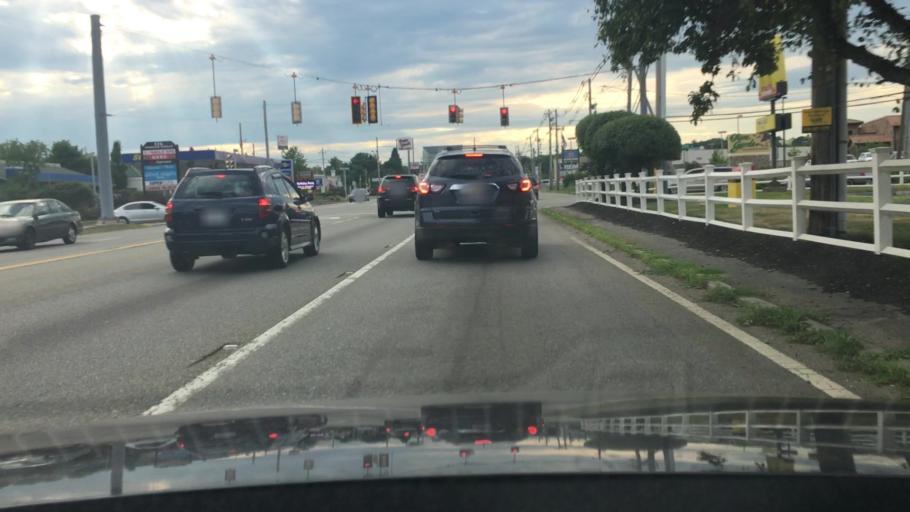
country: US
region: Massachusetts
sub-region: Essex County
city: Danvers
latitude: 42.5566
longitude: -70.9677
